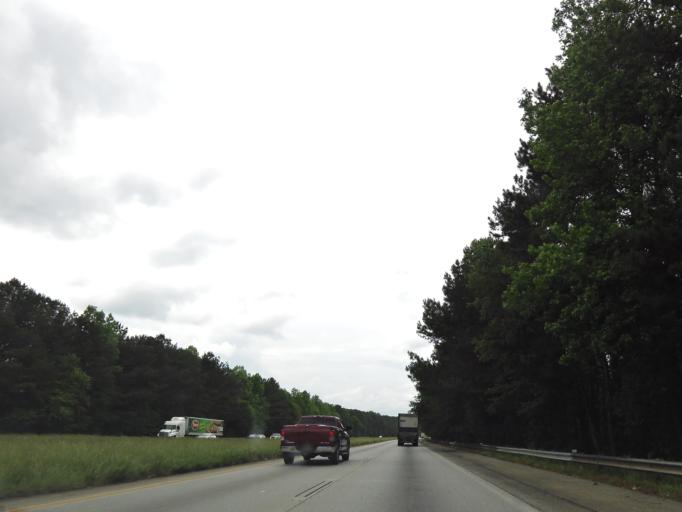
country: US
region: Georgia
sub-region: Carroll County
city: Temple
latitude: 33.7170
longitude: -84.9836
